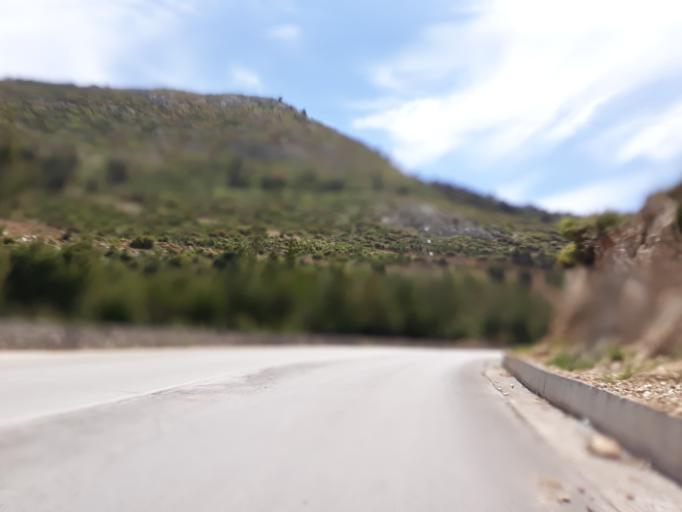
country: GR
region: Attica
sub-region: Nomarchia Dytikis Attikis
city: Magoula
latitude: 38.1708
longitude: 23.5474
